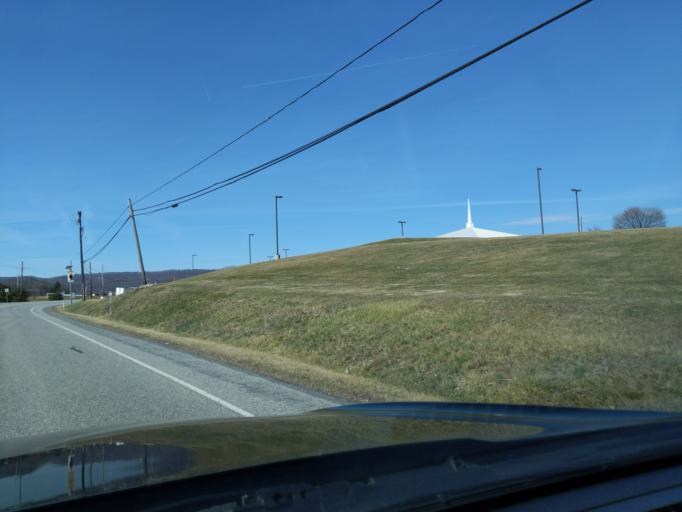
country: US
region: Pennsylvania
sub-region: Blair County
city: Roaring Spring
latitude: 40.3346
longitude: -78.3798
